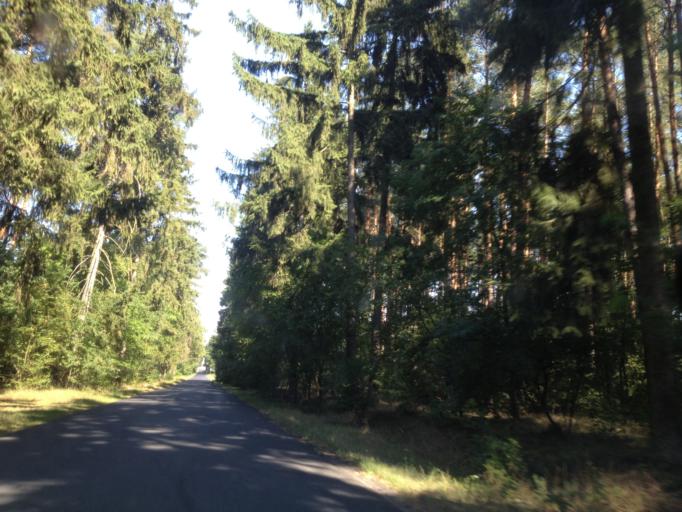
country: PL
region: Greater Poland Voivodeship
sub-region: Powiat sredzki
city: Zaniemysl
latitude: 52.1314
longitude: 17.1025
